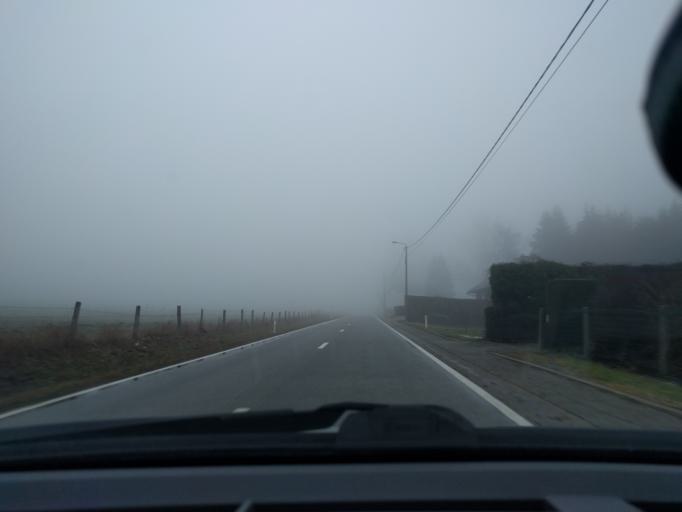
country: BE
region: Wallonia
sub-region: Province du Luxembourg
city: Gouvy
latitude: 50.1977
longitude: 5.9625
